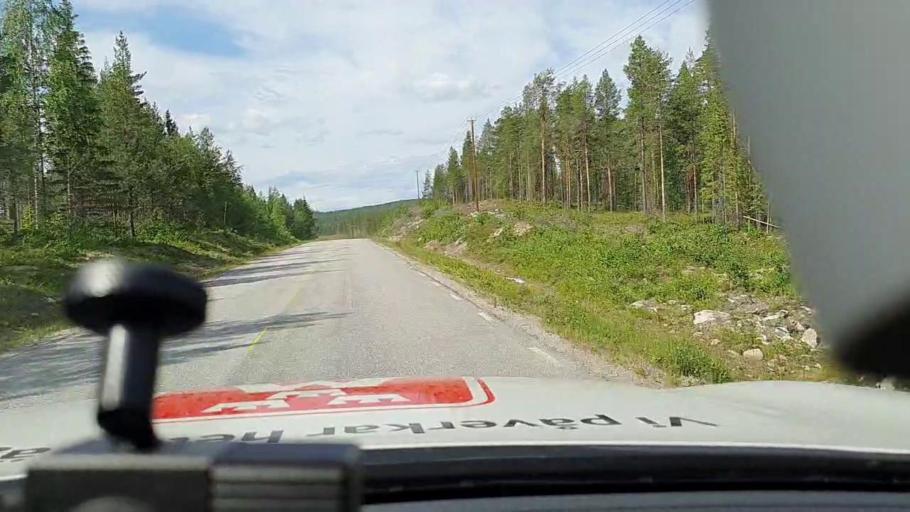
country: SE
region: Norrbotten
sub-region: Jokkmokks Kommun
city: Jokkmokk
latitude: 66.6236
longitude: 19.6732
